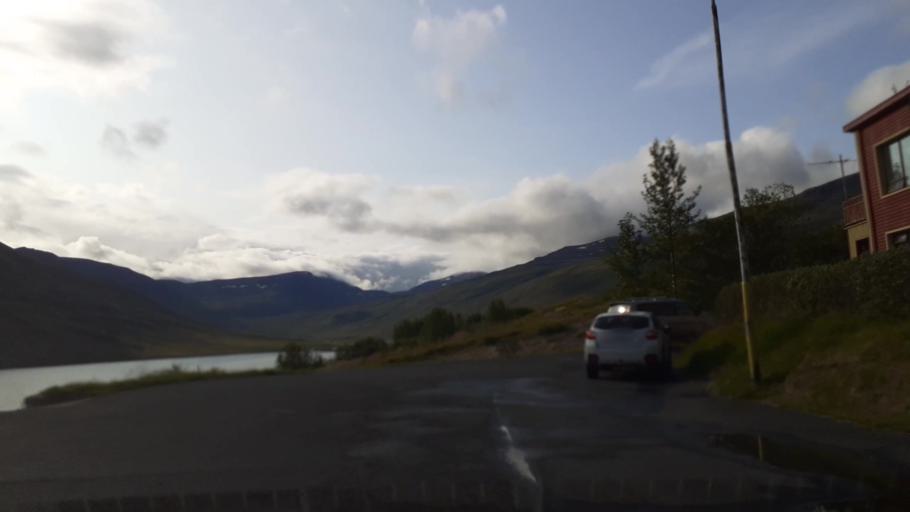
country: IS
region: East
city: Eskifjoerdur
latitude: 65.0664
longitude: -13.9997
